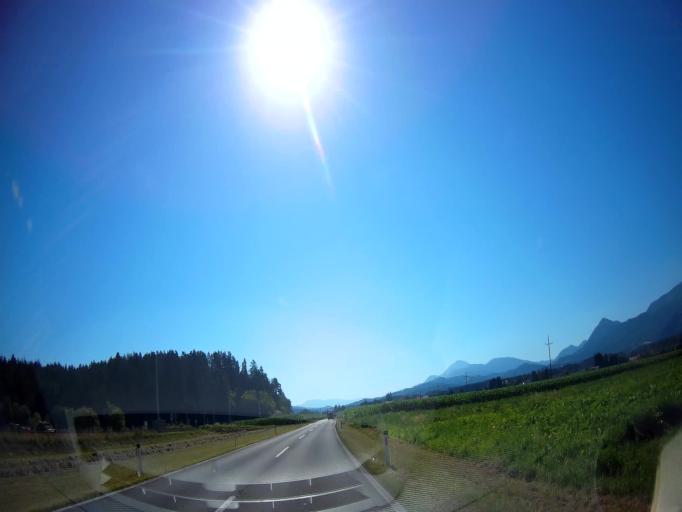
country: AT
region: Carinthia
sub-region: Politischer Bezirk Volkermarkt
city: Feistritz ob Bleiburg
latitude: 46.5782
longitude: 14.7634
